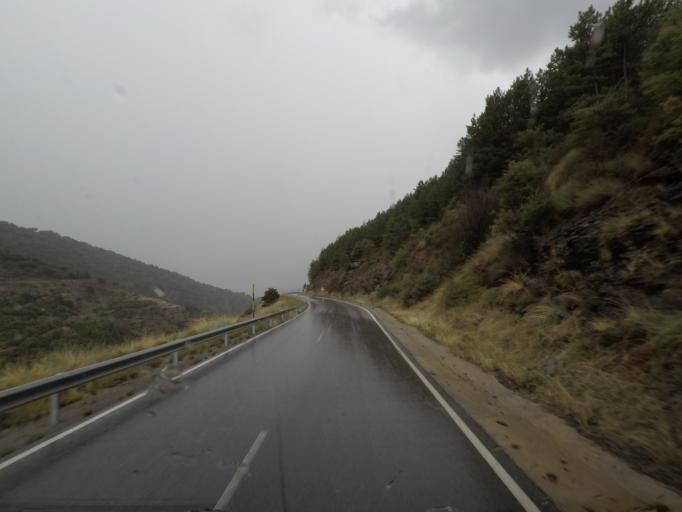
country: ES
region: Andalusia
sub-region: Provincia de Almeria
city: Bayarcal
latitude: 37.0688
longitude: -3.0173
